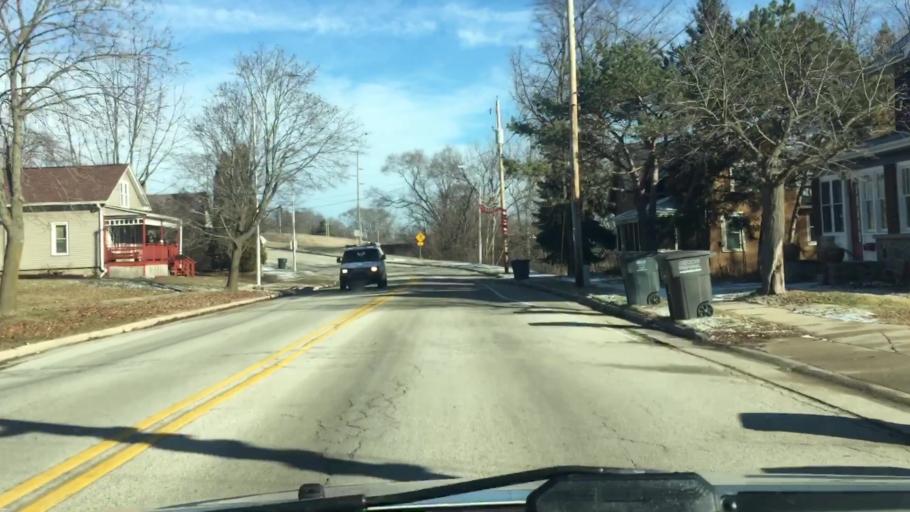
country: US
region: Wisconsin
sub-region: Waukesha County
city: Mukwonago
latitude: 42.8643
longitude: -88.3305
